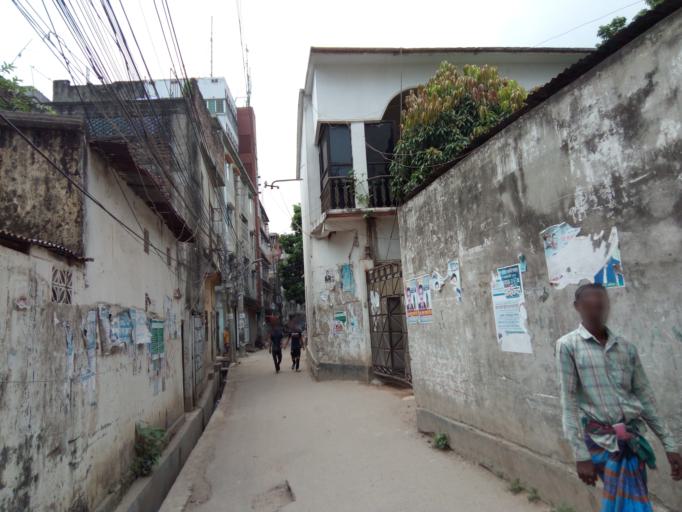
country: BD
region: Dhaka
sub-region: Dhaka
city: Dhaka
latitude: 23.7197
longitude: 90.4015
